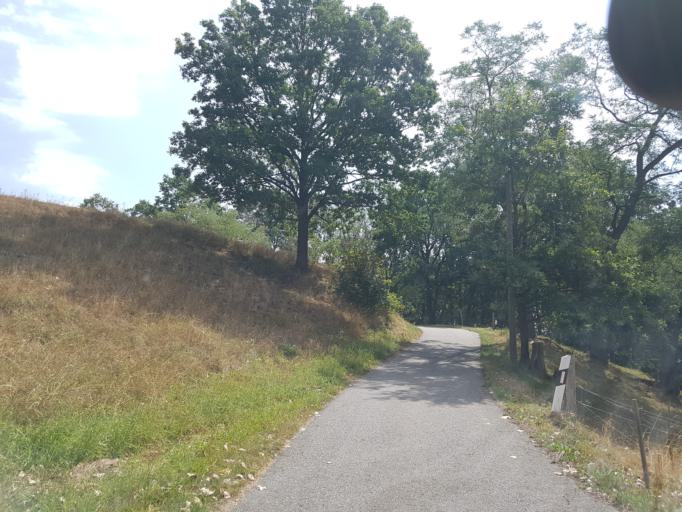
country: DE
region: Saxony
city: Waldheim
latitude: 51.0645
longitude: 12.9994
